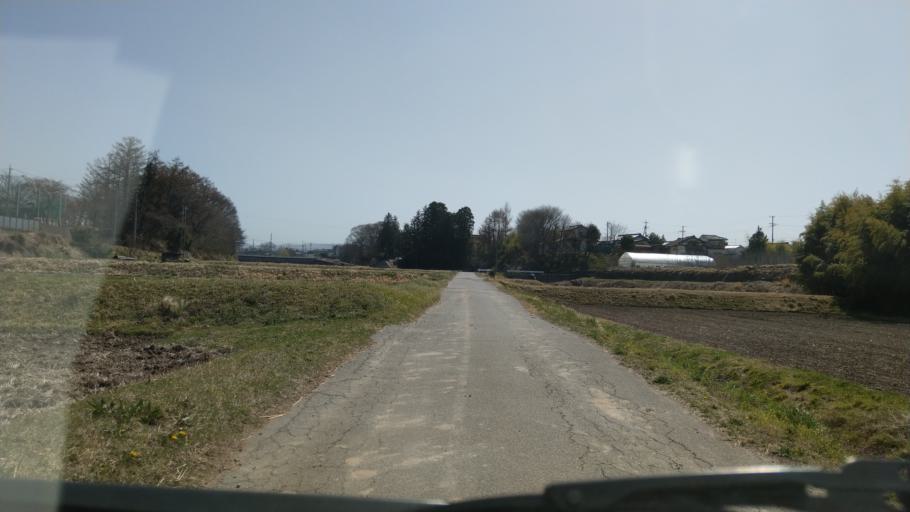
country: JP
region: Nagano
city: Komoro
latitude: 36.3000
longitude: 138.4329
